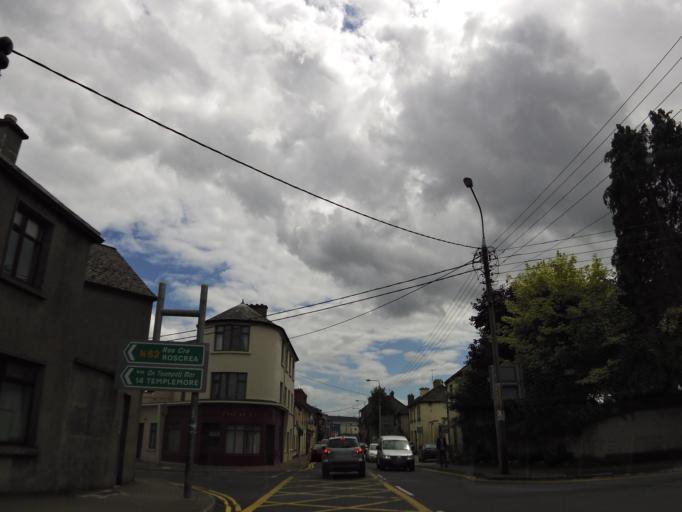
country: IE
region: Munster
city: Thurles
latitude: 52.6808
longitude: -7.8173
